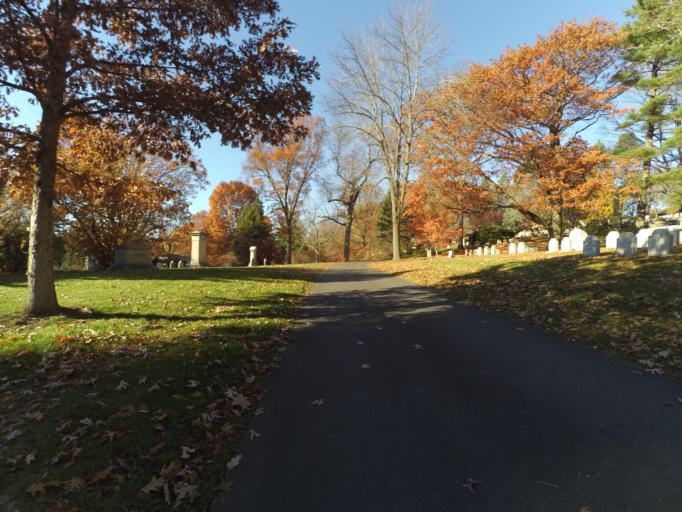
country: US
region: Massachusetts
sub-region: Middlesex County
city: Watertown
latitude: 42.3681
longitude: -71.1451
